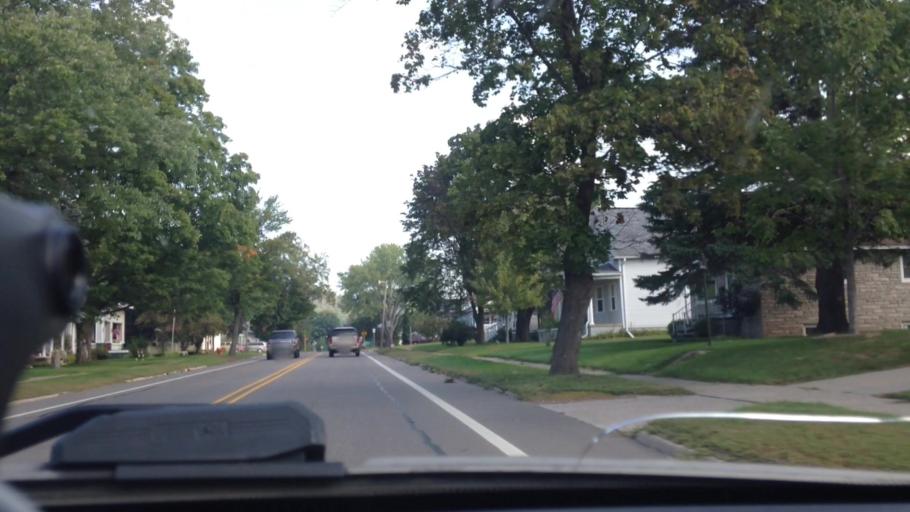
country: US
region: Michigan
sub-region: Dickinson County
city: Norway
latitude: 45.7839
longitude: -87.9098
